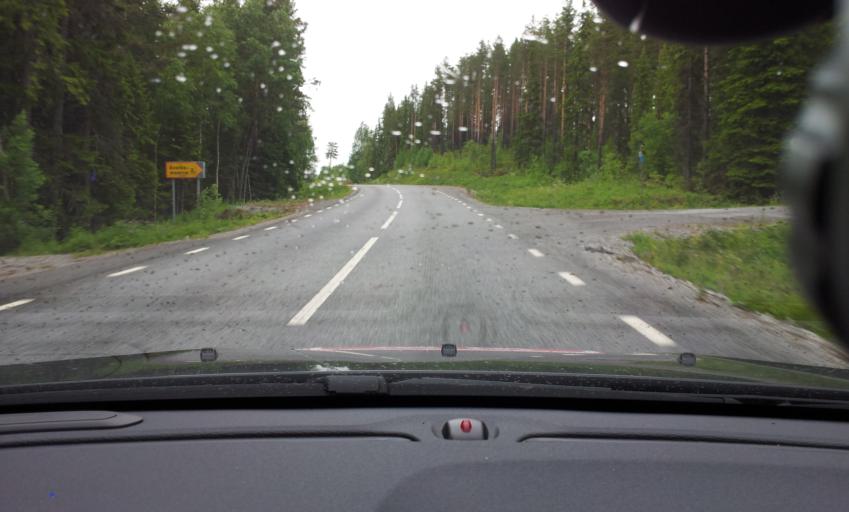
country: SE
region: Jaemtland
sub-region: OEstersunds Kommun
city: Lit
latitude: 63.7199
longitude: 14.7149
